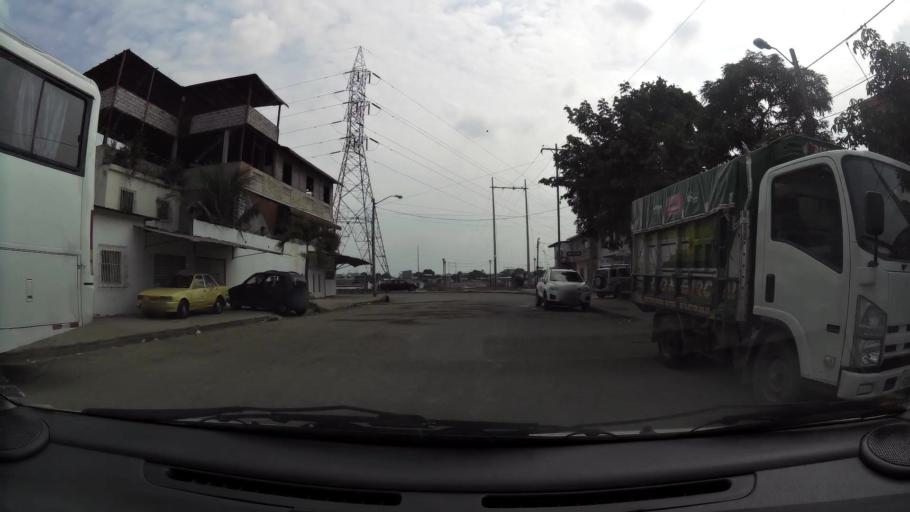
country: EC
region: Guayas
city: Guayaquil
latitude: -2.2410
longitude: -79.9103
